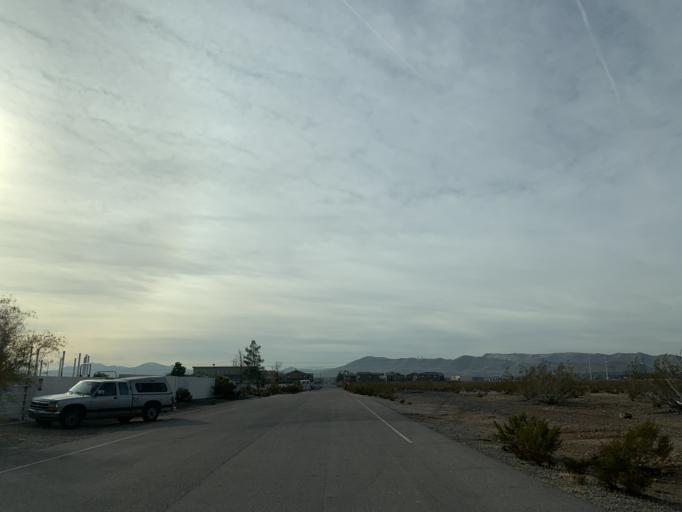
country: US
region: Nevada
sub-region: Clark County
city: Enterprise
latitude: 36.0087
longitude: -115.1857
